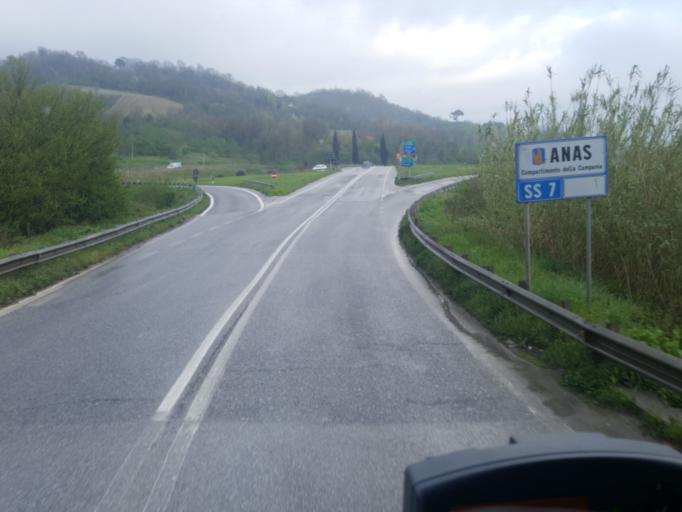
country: IT
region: Campania
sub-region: Provincia di Avellino
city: Manocalzati
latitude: 40.9377
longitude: 14.8297
